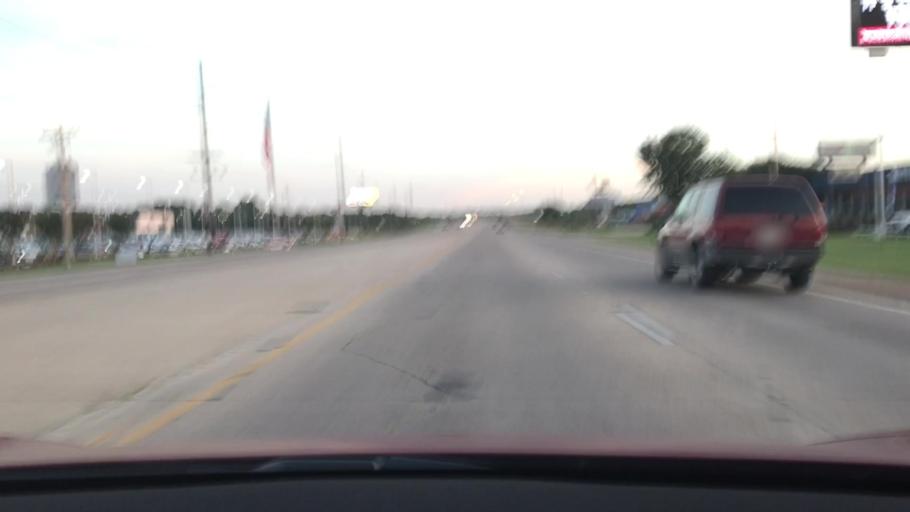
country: US
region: Louisiana
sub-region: Bossier Parish
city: Bossier City
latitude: 32.4191
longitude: -93.7219
